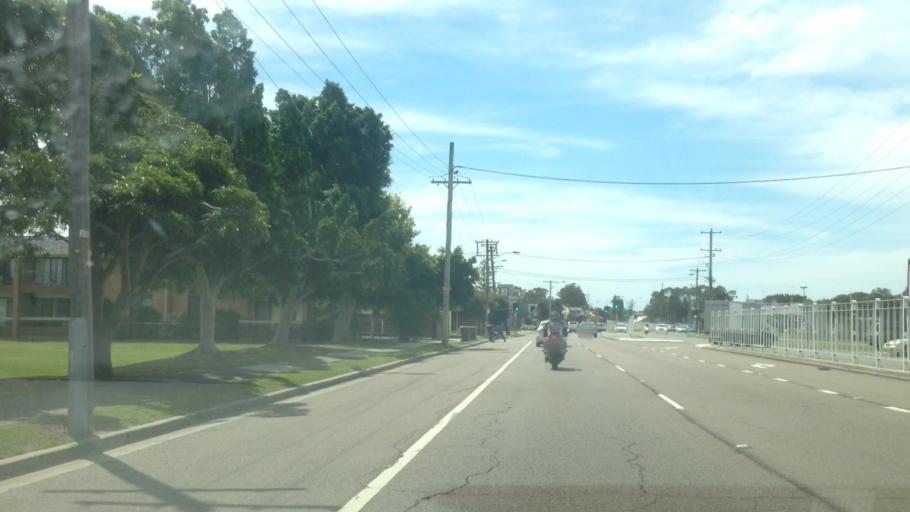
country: AU
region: New South Wales
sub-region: Newcastle
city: Broadmeadow
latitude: -32.9193
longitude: 151.7241
